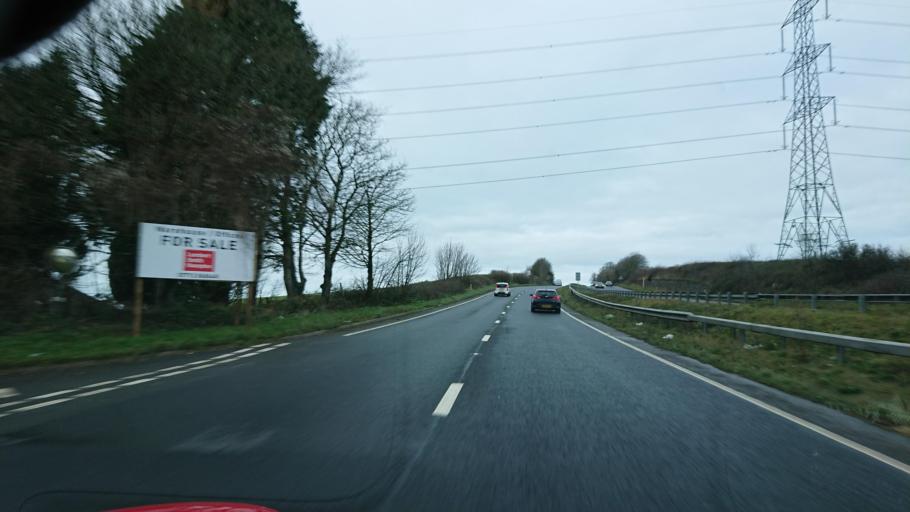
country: GB
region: England
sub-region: Cornwall
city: Liskeard
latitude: 50.4359
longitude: -4.4401
